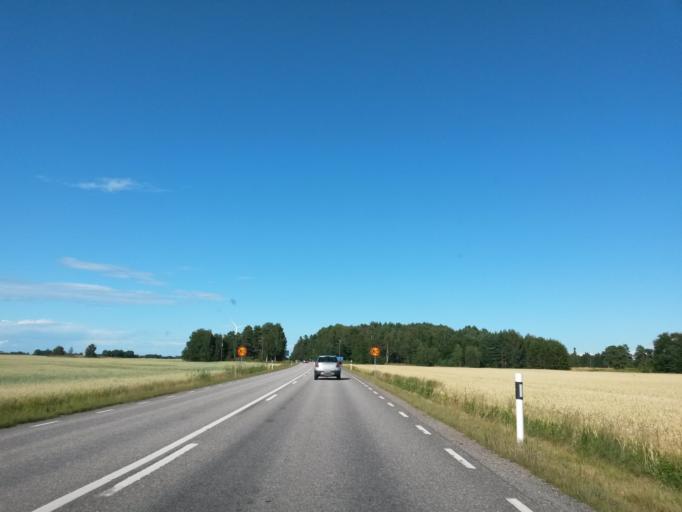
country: SE
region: Vaestra Goetaland
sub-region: Grastorps Kommun
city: Graestorp
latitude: 58.3351
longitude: 12.6129
